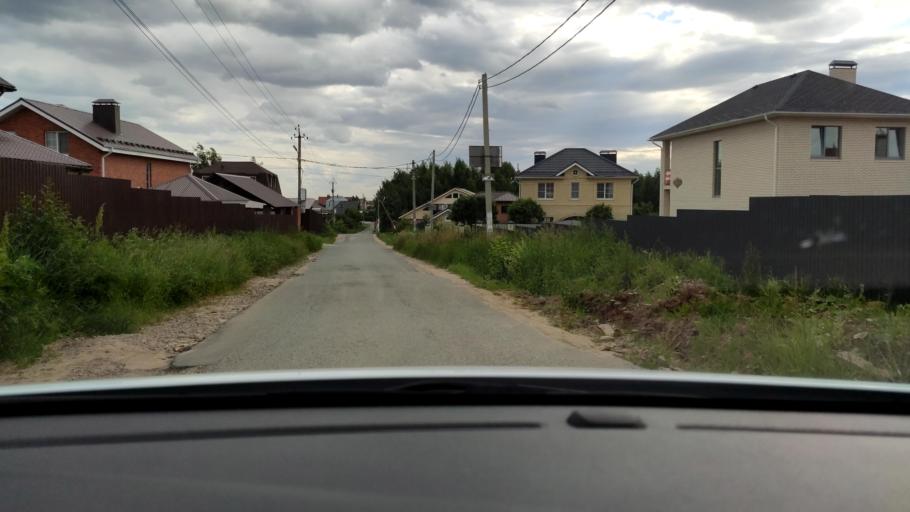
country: RU
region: Tatarstan
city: Stolbishchi
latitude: 55.7607
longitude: 49.2969
